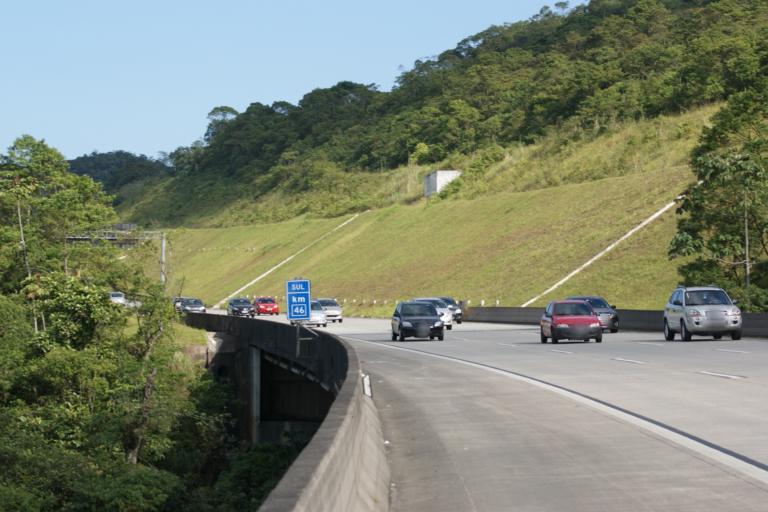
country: BR
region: Sao Paulo
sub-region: Cubatao
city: Cubatao
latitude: -23.9255
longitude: -46.5404
